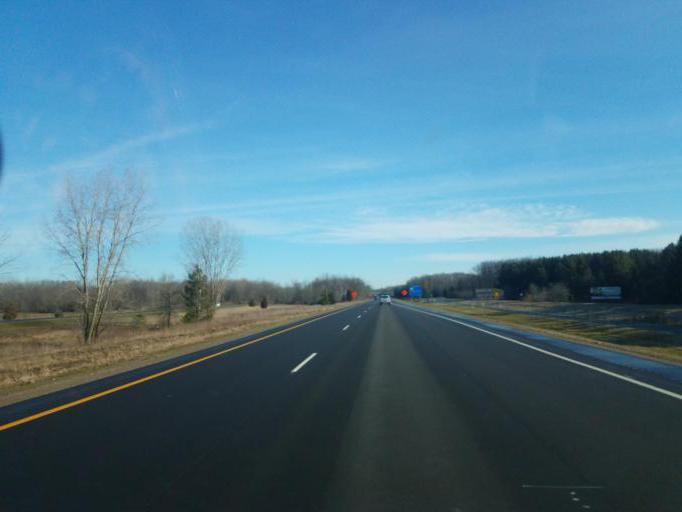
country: US
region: Michigan
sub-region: Gratiot County
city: Saint Louis
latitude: 43.3575
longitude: -84.6010
